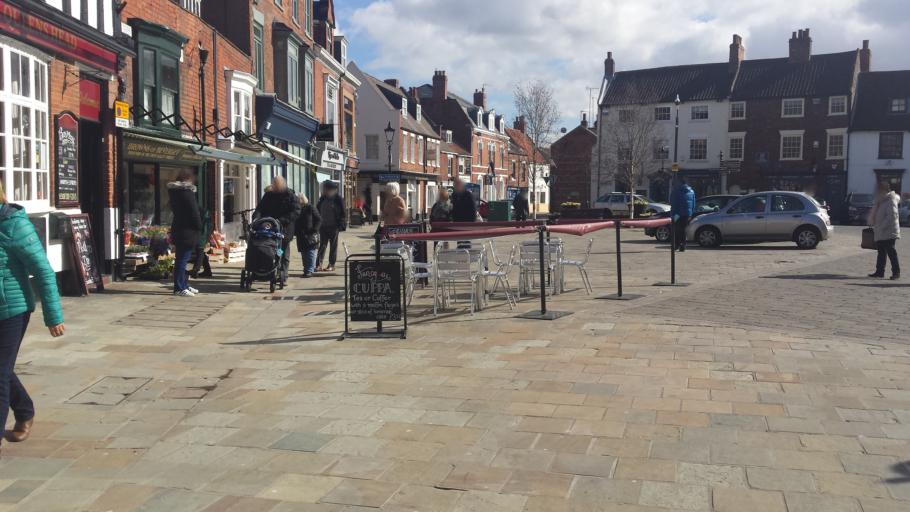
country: GB
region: England
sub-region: East Riding of Yorkshire
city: Beverley
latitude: 53.8413
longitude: -0.4270
